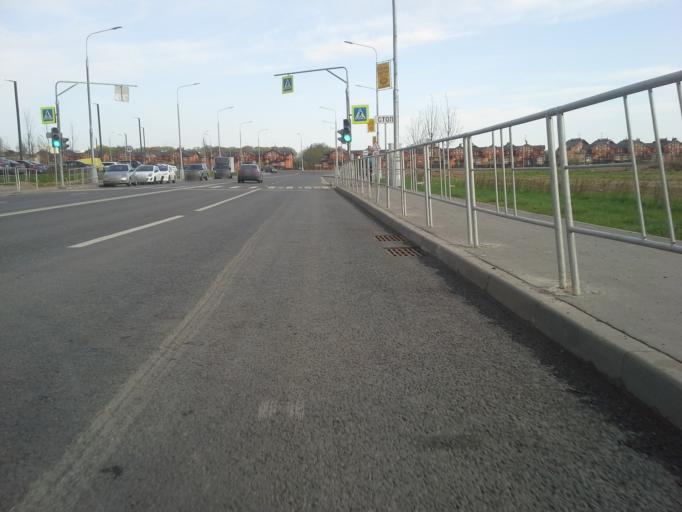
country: RU
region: Moskovskaya
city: Kommunarka
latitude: 55.5408
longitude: 37.4793
